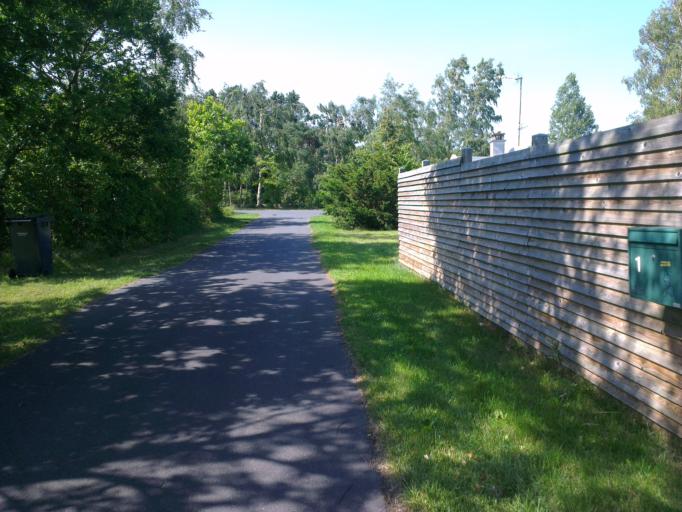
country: DK
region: Capital Region
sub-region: Halsnaes Kommune
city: Hundested
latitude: 55.9191
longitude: 11.9087
